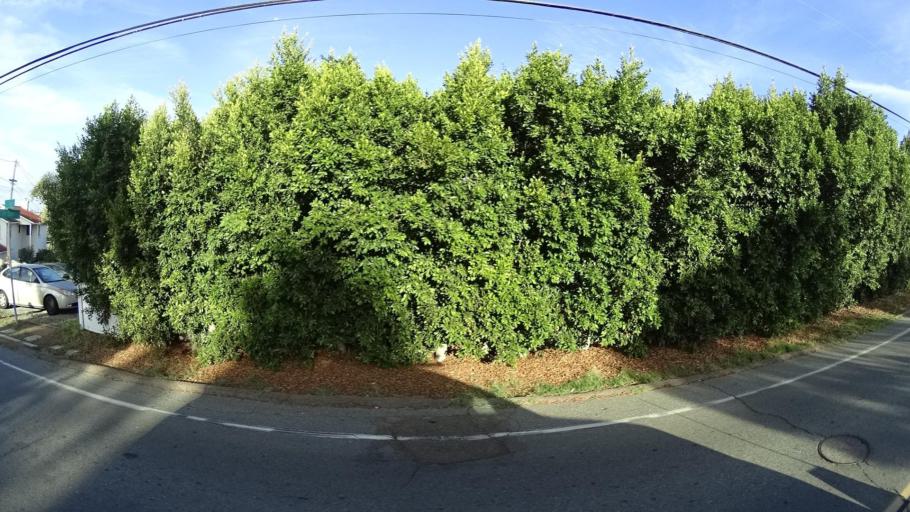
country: US
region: California
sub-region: San Diego County
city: La Presa
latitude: 32.7201
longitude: -117.0090
